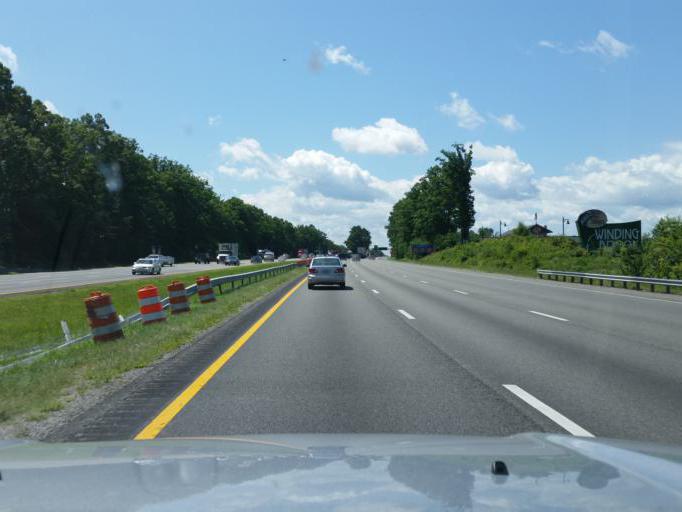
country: US
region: Virginia
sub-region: Hanover County
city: Ashland
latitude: 37.7158
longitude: -77.4480
